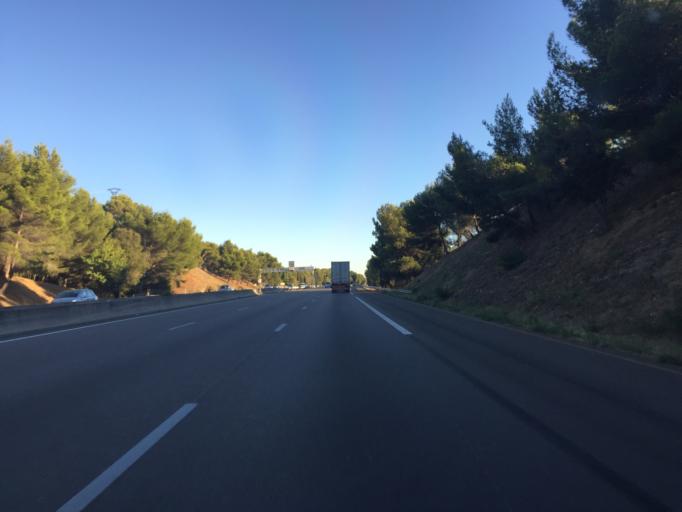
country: FR
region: Provence-Alpes-Cote d'Azur
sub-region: Departement des Bouches-du-Rhone
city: Salon-de-Provence
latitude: 43.6517
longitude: 5.1082
